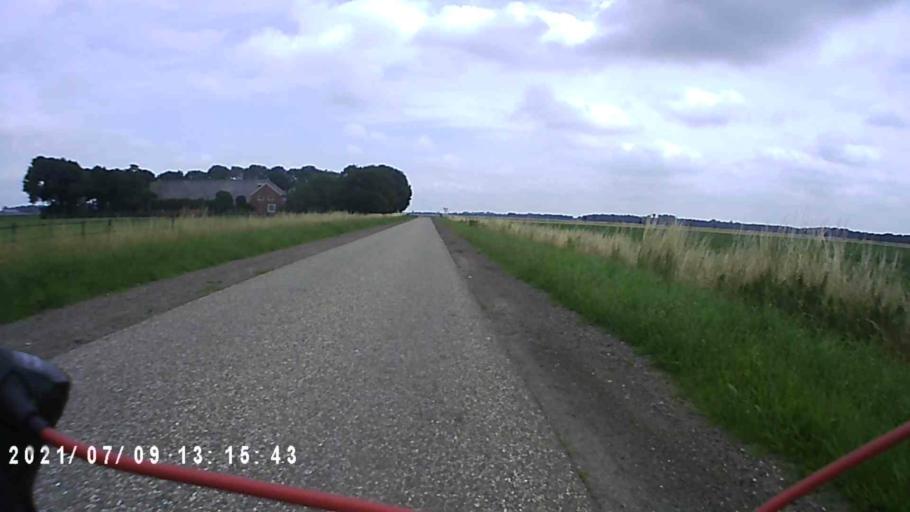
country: NL
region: Groningen
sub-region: Gemeente Vlagtwedde
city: Vlagtwedde
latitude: 53.1199
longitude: 7.1429
